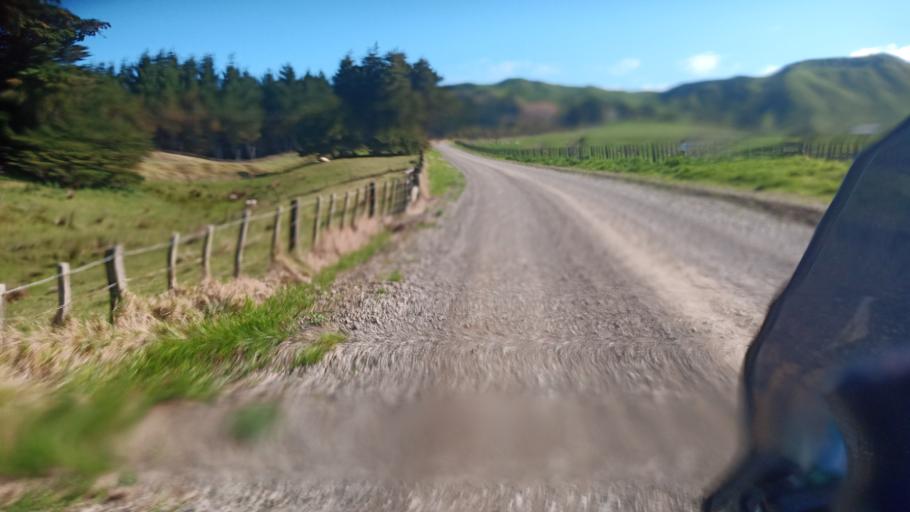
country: NZ
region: Gisborne
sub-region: Gisborne District
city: Gisborne
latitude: -39.1533
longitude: 177.9189
